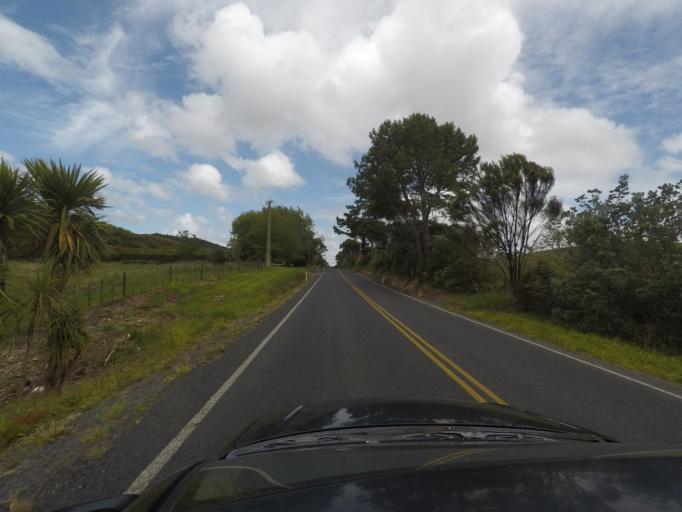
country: NZ
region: Auckland
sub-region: Auckland
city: Parakai
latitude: -36.6465
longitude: 174.5170
